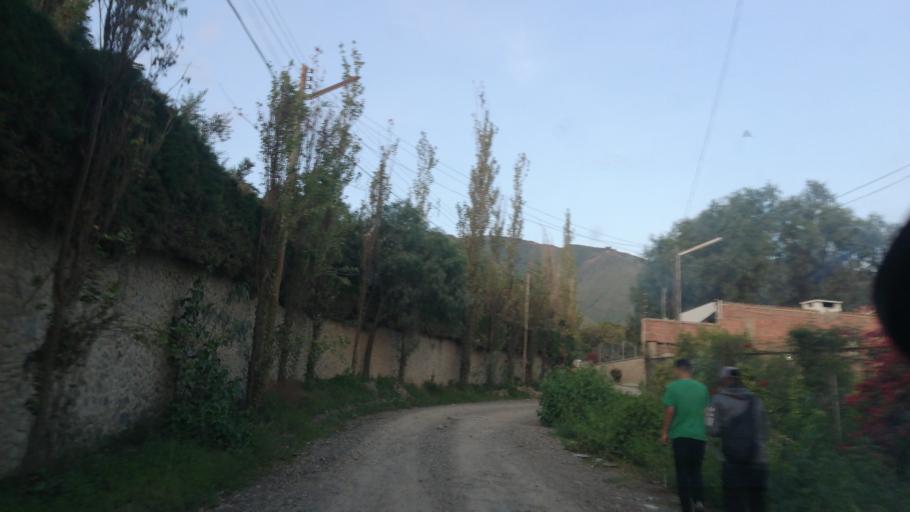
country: BO
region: Cochabamba
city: Cochabamba
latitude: -17.3343
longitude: -66.2090
